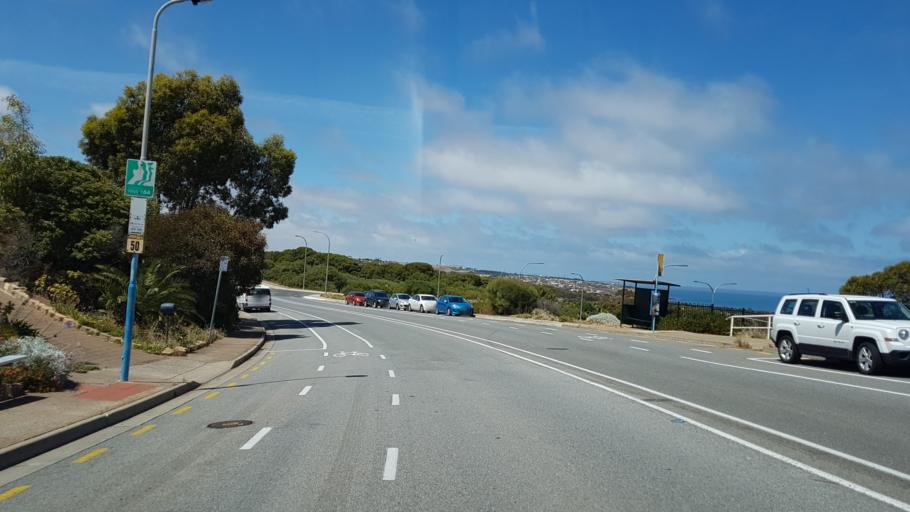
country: AU
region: South Australia
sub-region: Marion
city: Marino
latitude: -35.0671
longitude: 138.5065
